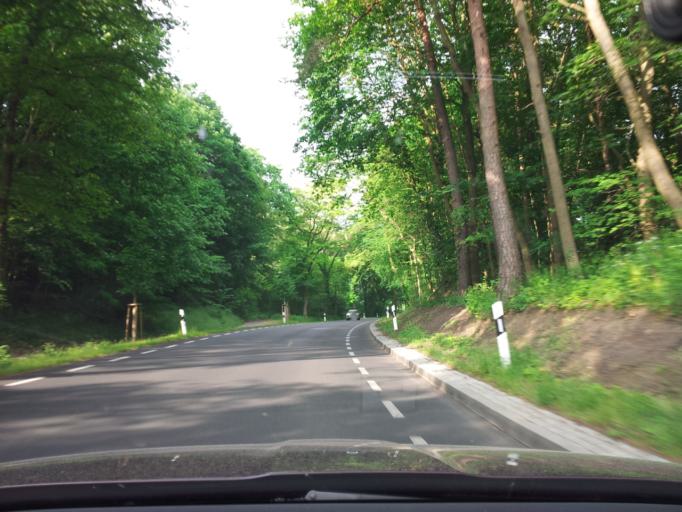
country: DE
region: Brandenburg
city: Werder
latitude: 52.3323
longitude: 12.9294
